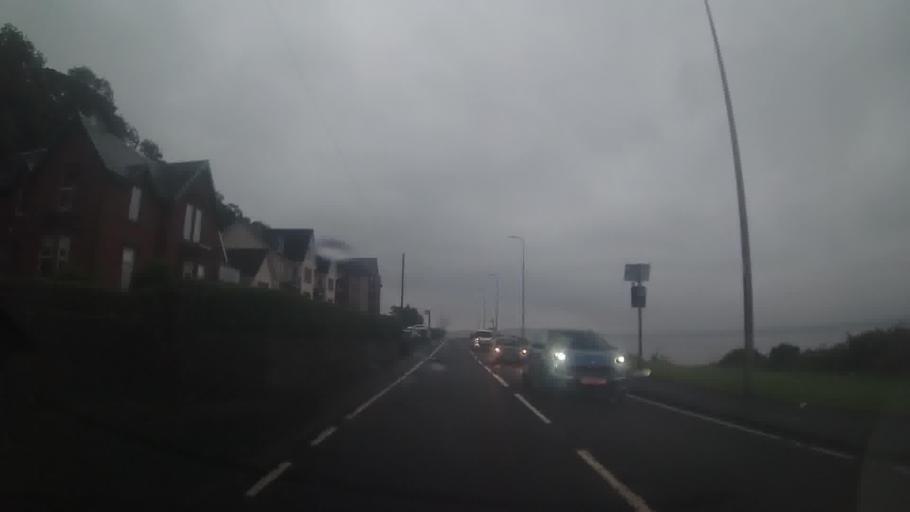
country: GB
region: Scotland
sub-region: North Ayrshire
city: Skelmorlie
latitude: 55.8656
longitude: -4.8914
